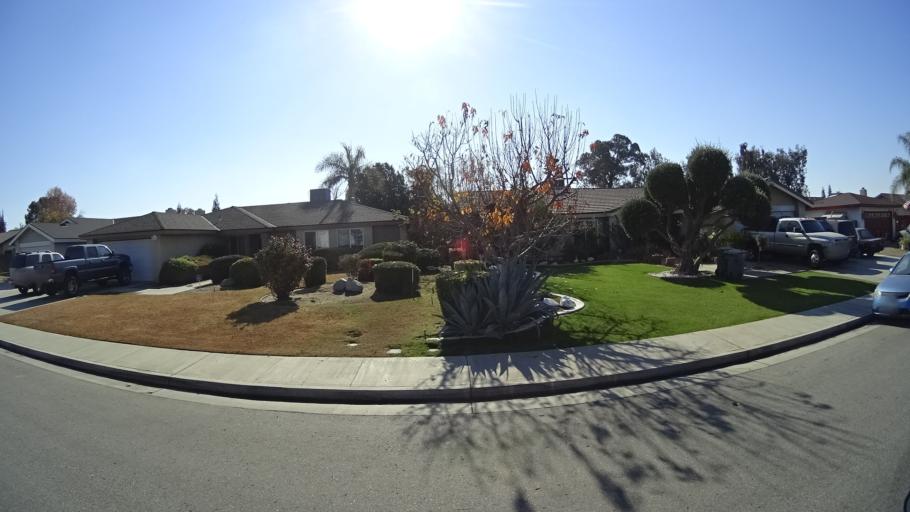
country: US
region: California
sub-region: Kern County
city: Greenfield
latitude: 35.2982
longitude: -119.0539
